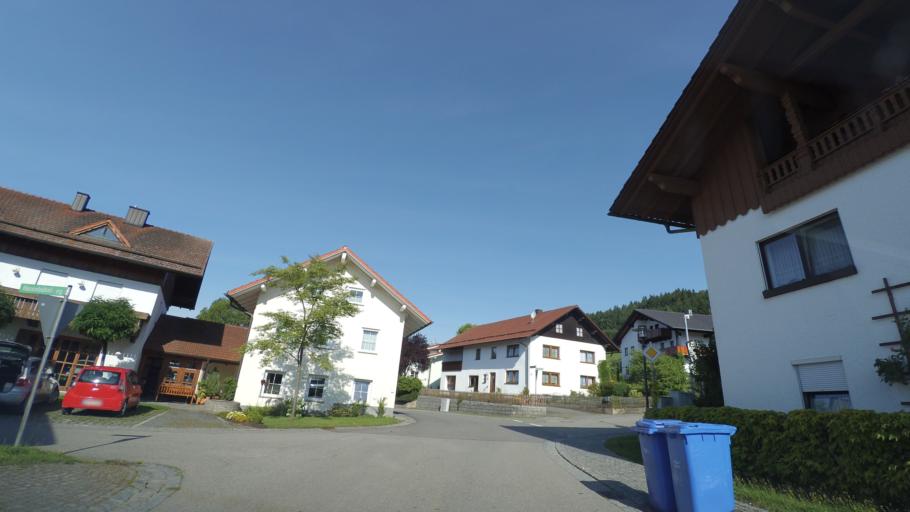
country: DE
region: Bavaria
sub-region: Lower Bavaria
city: Geiersthal
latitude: 49.0570
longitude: 12.9684
